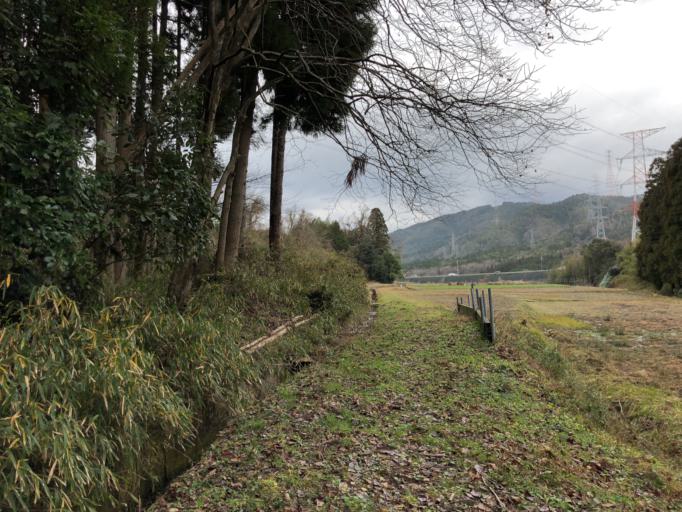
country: JP
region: Kyoto
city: Kameoka
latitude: 34.9918
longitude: 135.6208
